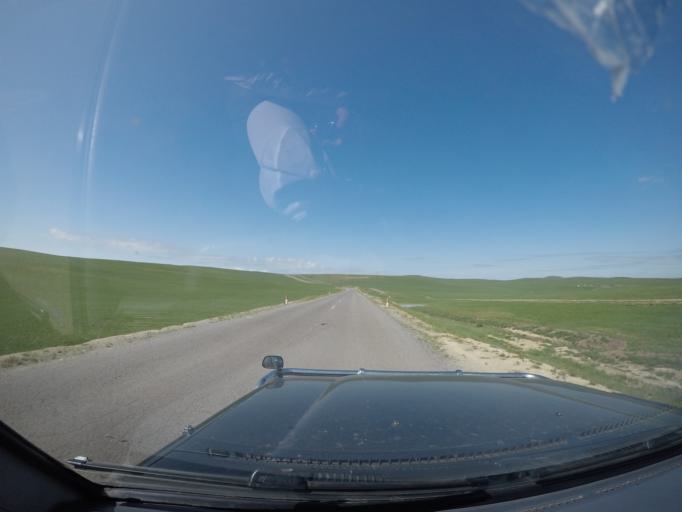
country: MN
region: Suhbaatar
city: Bayasgalant
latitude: 47.3541
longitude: 111.6648
